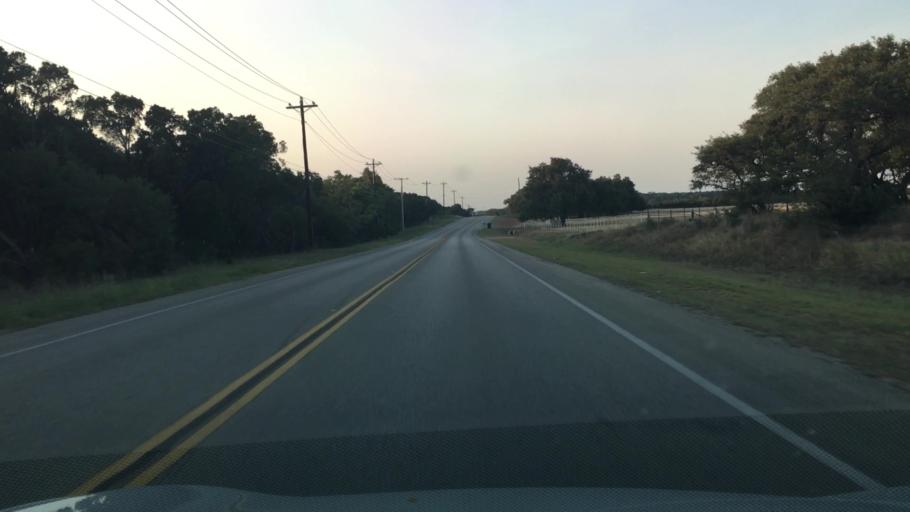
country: US
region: Texas
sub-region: Hays County
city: Dripping Springs
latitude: 30.1566
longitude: -98.0091
